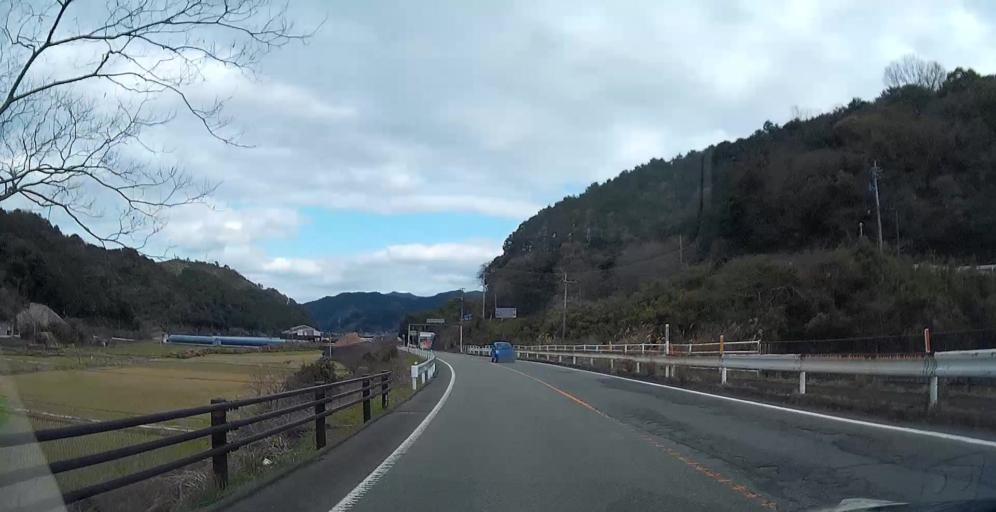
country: JP
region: Kumamoto
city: Minamata
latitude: 32.3380
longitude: 130.4920
